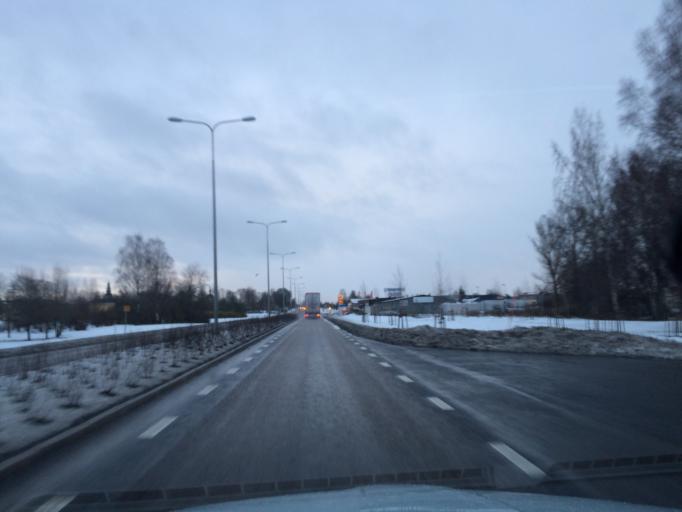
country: SE
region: Vaestmanland
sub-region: Kopings Kommun
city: Koping
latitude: 59.5180
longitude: 15.9732
